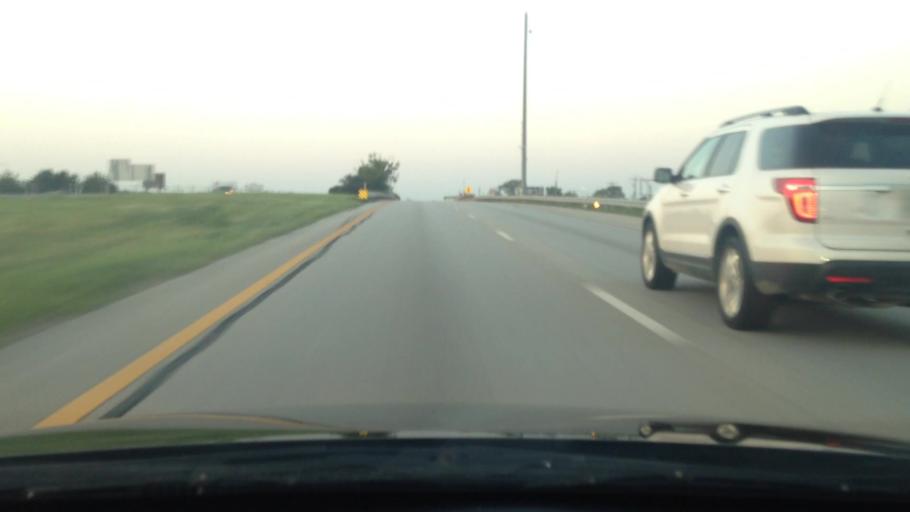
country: US
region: Texas
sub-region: Tarrant County
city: Forest Hill
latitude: 32.7068
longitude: -97.2320
